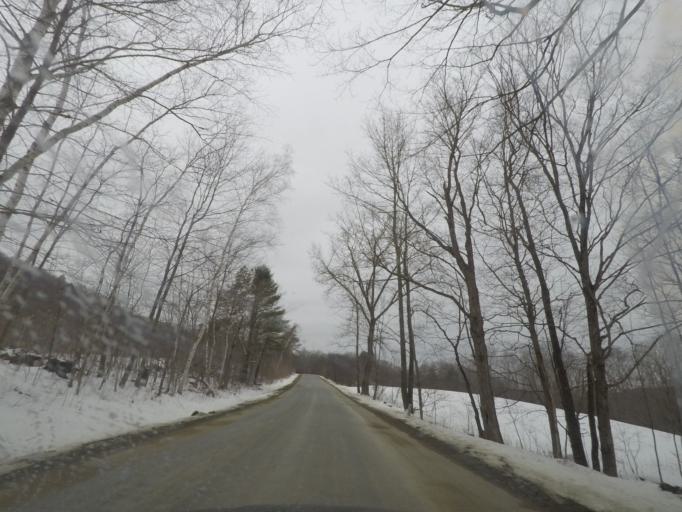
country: US
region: New York
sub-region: Rensselaer County
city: Averill Park
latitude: 42.5595
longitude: -73.4125
